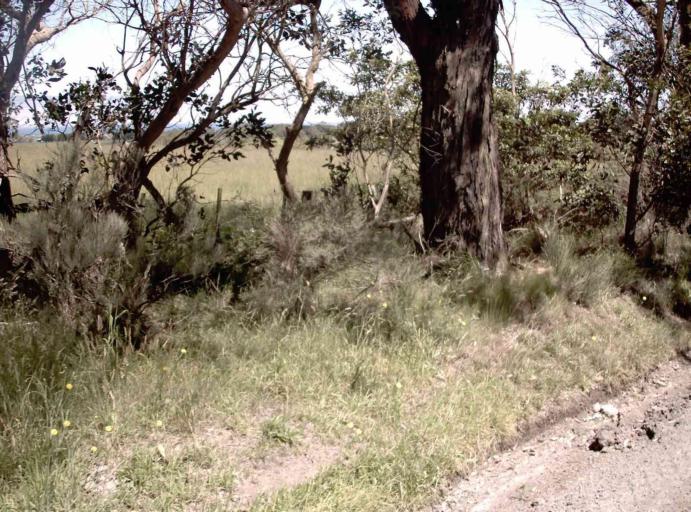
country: AU
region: Victoria
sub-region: Bass Coast
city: North Wonthaggi
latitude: -38.7614
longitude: 146.0683
